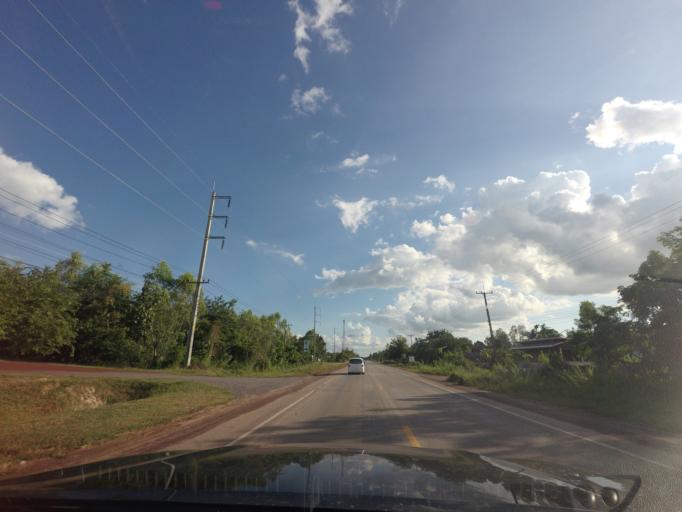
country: TH
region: Changwat Udon Thani
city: Thung Fon
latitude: 17.4855
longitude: 103.1965
